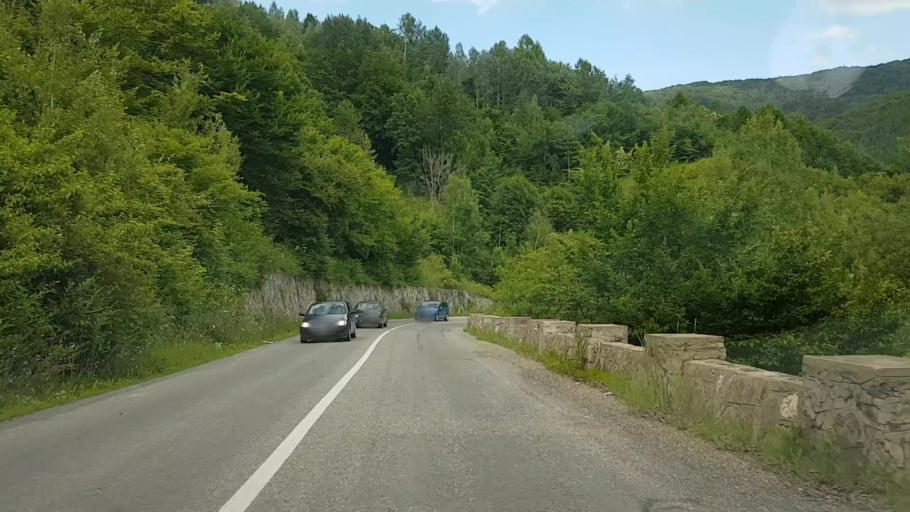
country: RO
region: Neamt
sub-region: Comuna Pangarati
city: Pangarati
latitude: 46.9895
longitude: 26.1143
